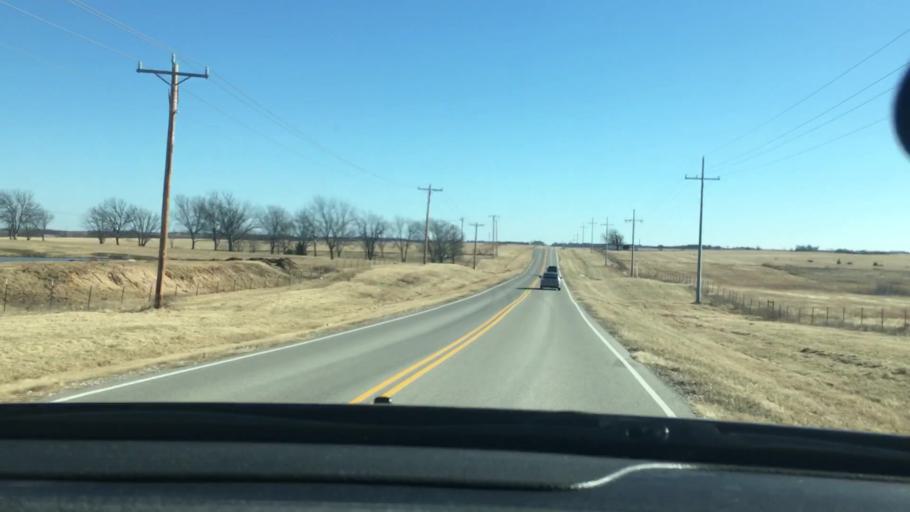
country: US
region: Oklahoma
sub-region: Murray County
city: Davis
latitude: 34.4773
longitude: -97.1022
